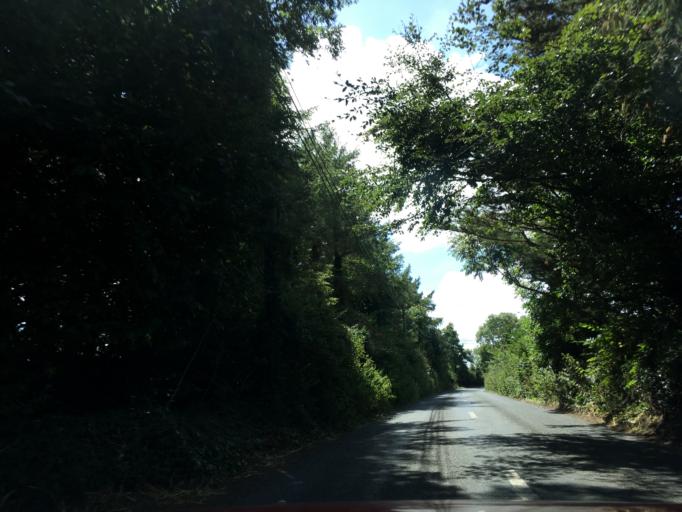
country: IE
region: Munster
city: Cahir
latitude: 52.3442
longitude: -7.9466
